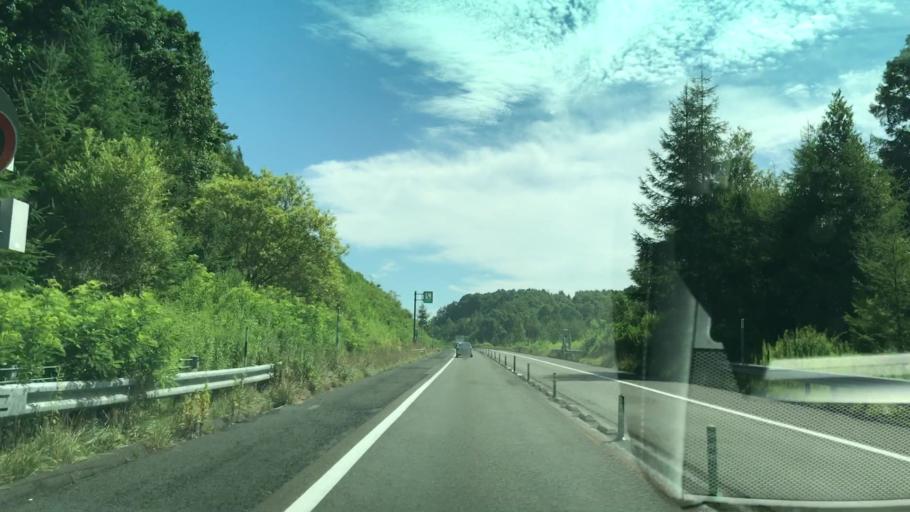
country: JP
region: Hokkaido
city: Chitose
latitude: 42.8994
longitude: 141.8807
